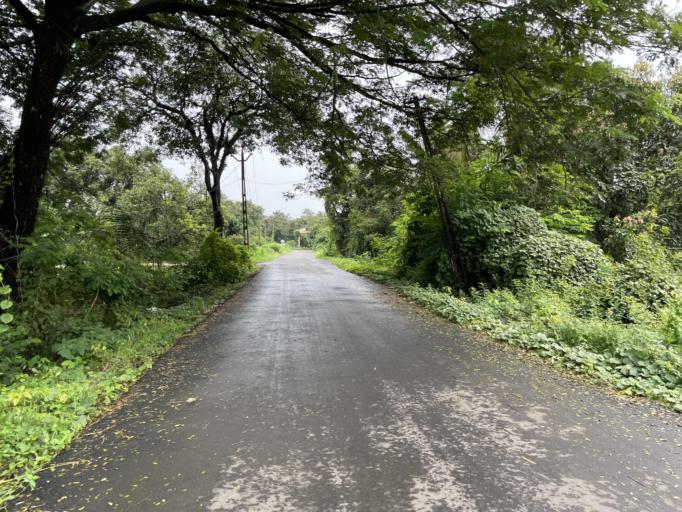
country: IN
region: Gujarat
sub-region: Valsad
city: Pardi
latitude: 20.4524
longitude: 72.9346
